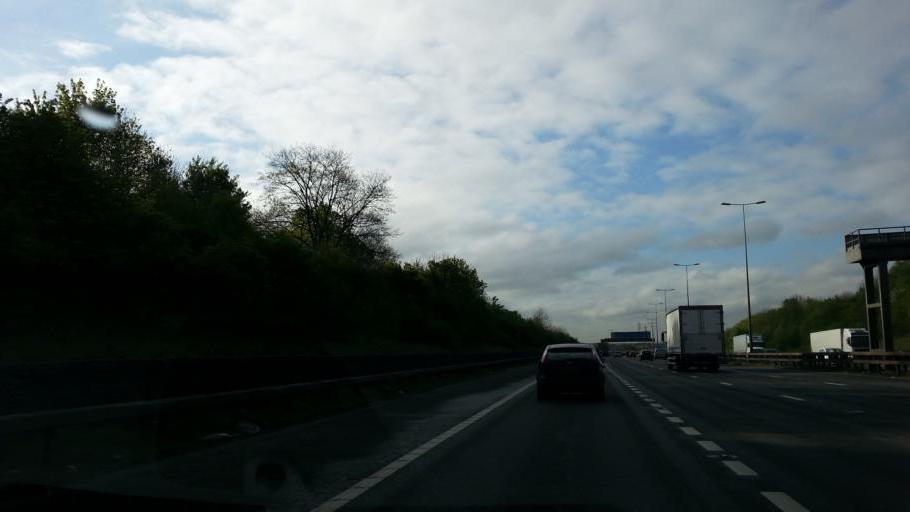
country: GB
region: England
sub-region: Leicestershire
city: Enderby
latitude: 52.6105
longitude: -1.1991
